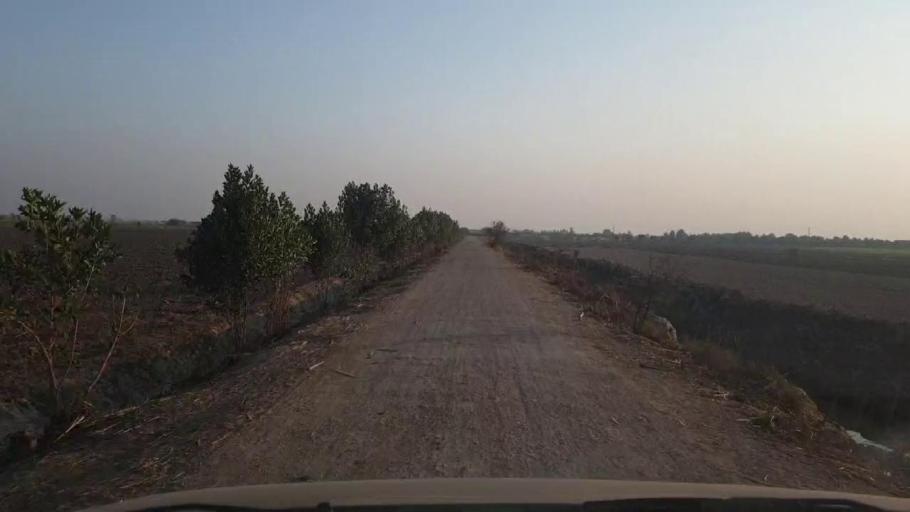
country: PK
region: Sindh
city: Mirwah Gorchani
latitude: 25.3495
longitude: 69.1533
